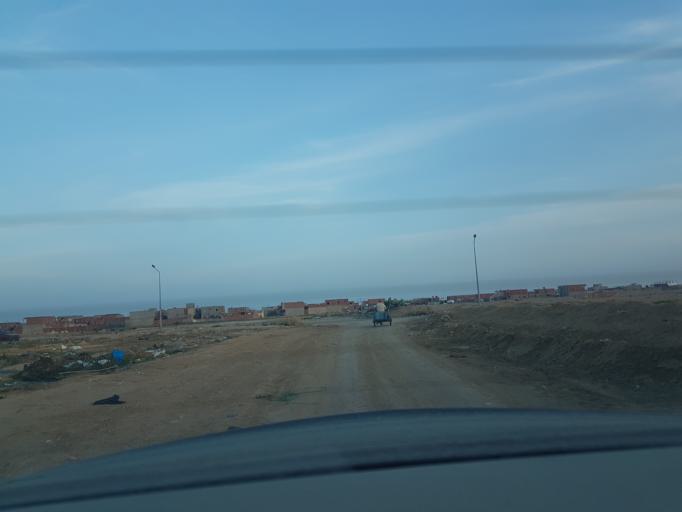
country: TN
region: Safaqis
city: Sfax
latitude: 34.7022
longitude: 10.6980
